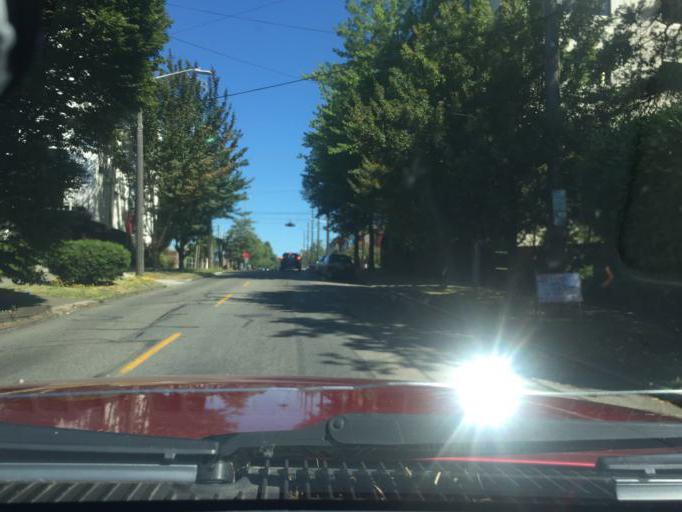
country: US
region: Washington
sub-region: King County
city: Seattle
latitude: 47.6055
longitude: -122.3142
